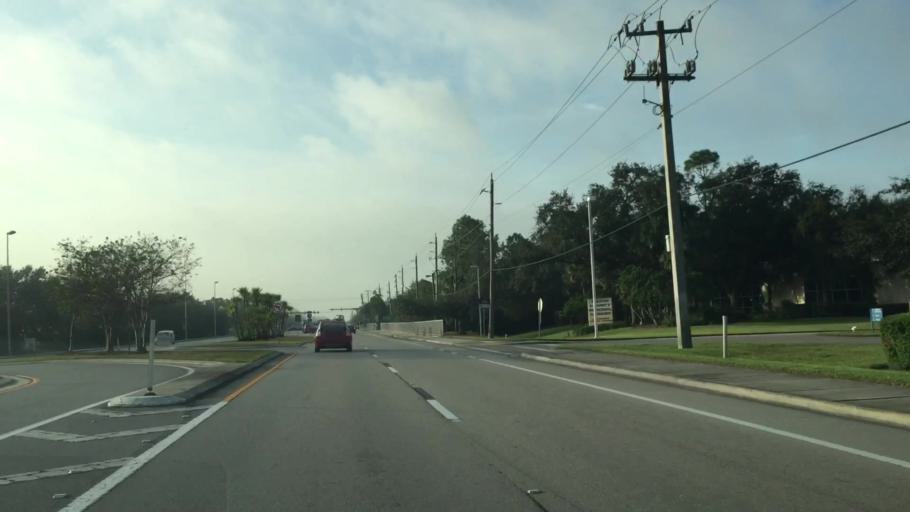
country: US
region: Florida
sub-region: Lee County
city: Estero
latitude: 26.4343
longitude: -81.7886
